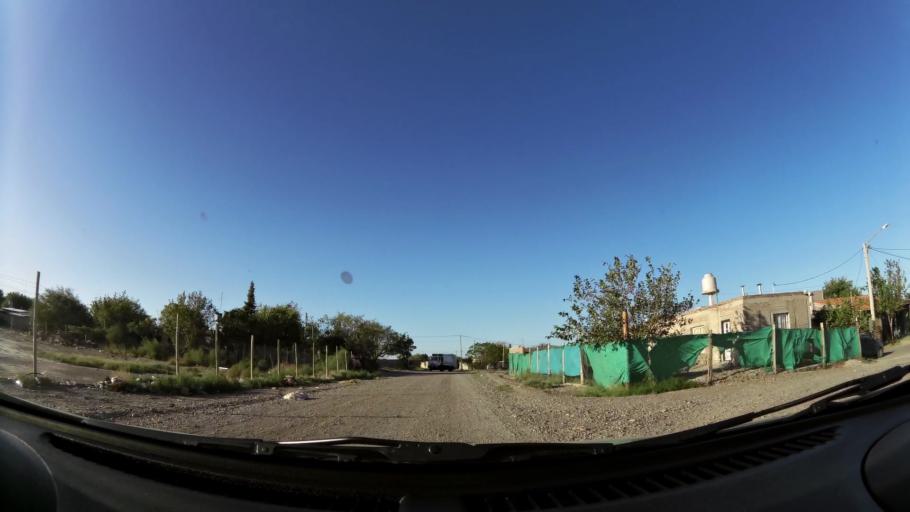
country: AR
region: San Juan
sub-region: Departamento de Santa Lucia
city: Santa Lucia
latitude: -31.5501
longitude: -68.5103
